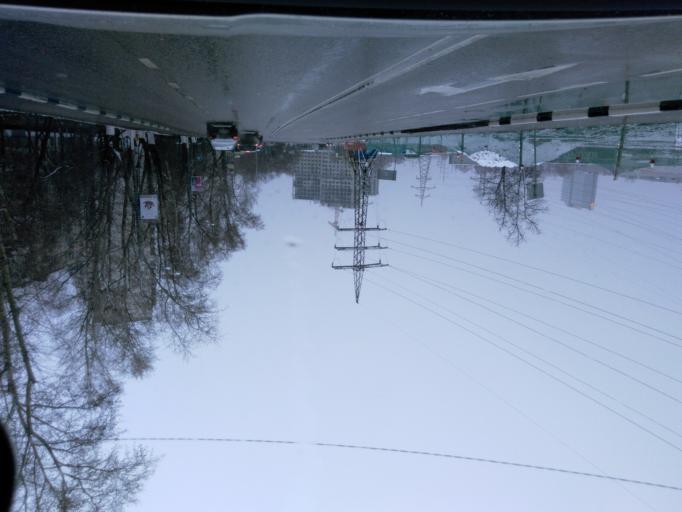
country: RU
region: Moscow
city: Khimki
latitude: 55.9005
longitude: 37.4170
